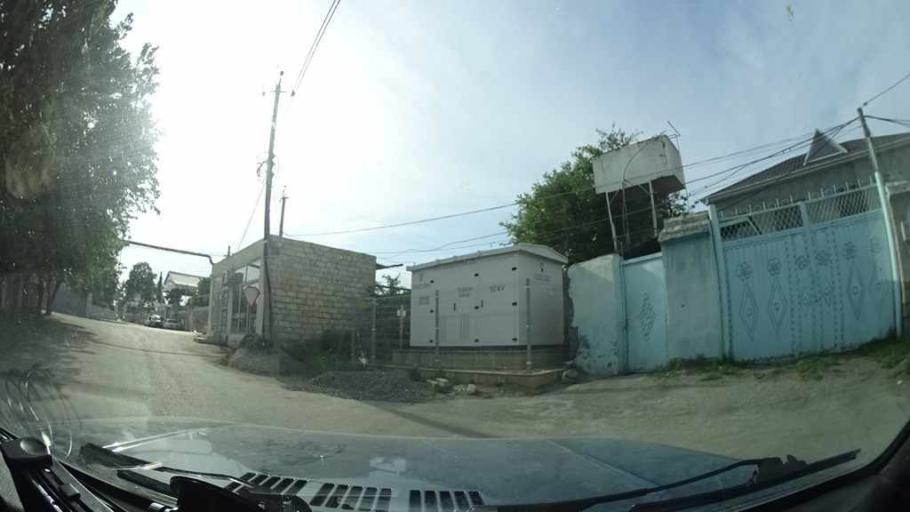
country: AZ
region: Barda Rayon
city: Barda
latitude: 40.3822
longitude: 47.1276
